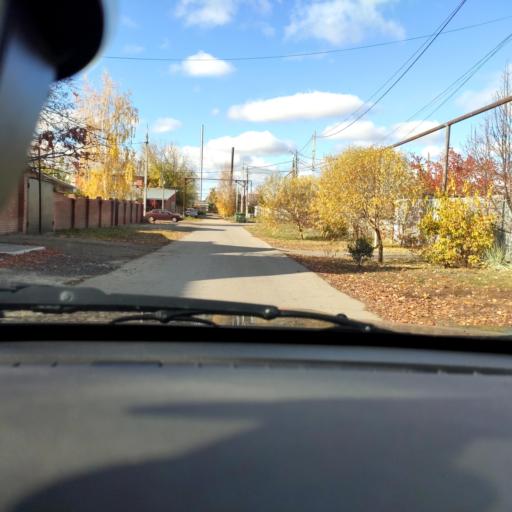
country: RU
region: Samara
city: Podstepki
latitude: 53.5098
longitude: 49.2326
